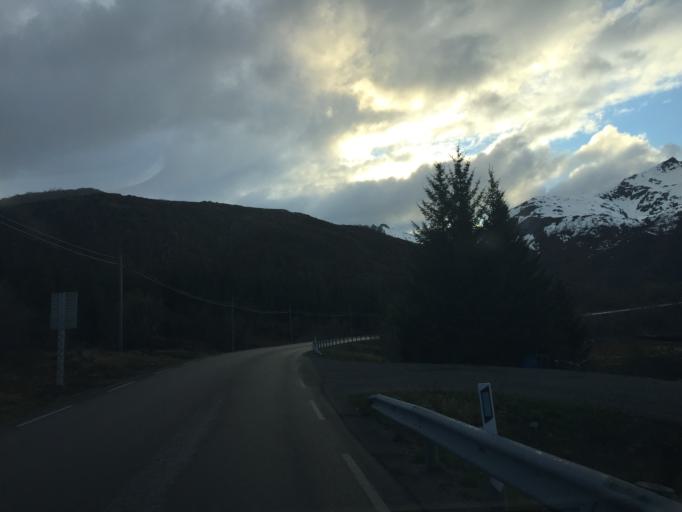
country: NO
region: Nordland
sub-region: Vagan
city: Svolvaer
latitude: 68.3190
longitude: 14.7030
